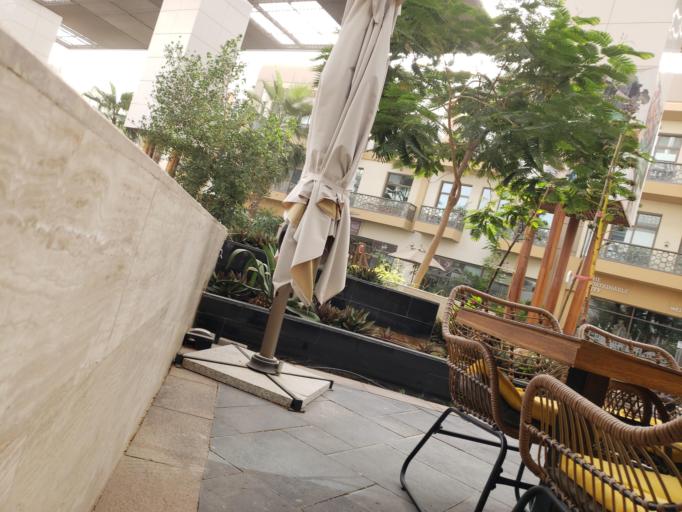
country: AE
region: Dubai
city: Dubai
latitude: 25.0279
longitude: 55.2755
